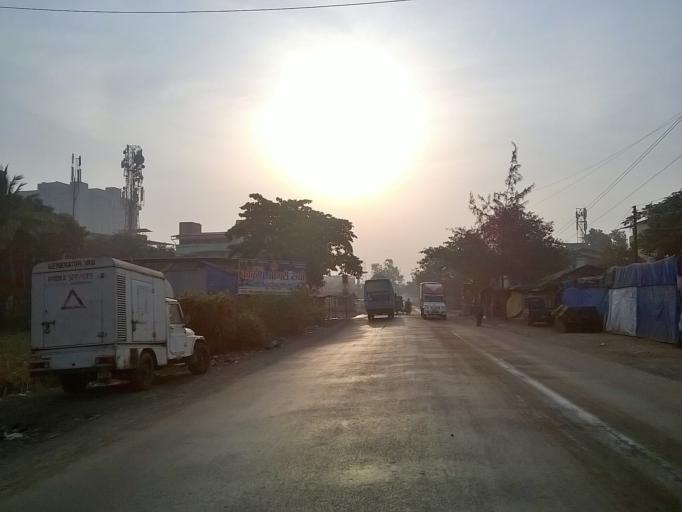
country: IN
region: Maharashtra
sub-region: Raigarh
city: Kalundri
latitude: 19.0005
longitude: 73.1328
